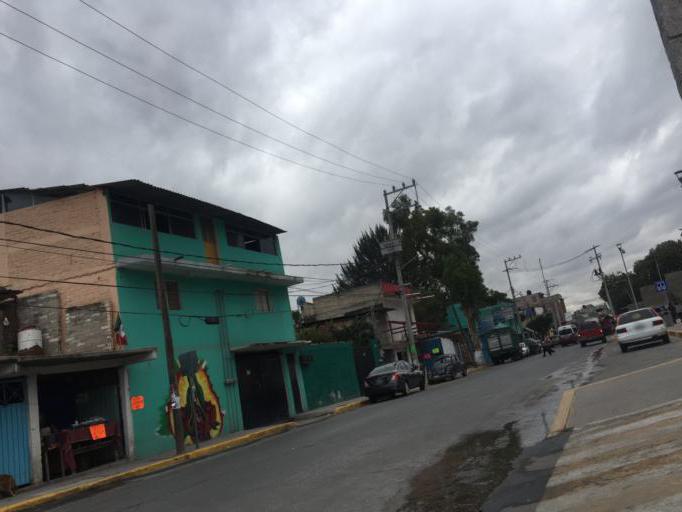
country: MX
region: Mexico
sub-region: Tlalnepantla de Baz
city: Puerto Escondido (Tepeolulco Puerto Escondido)
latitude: 19.5660
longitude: -99.0881
